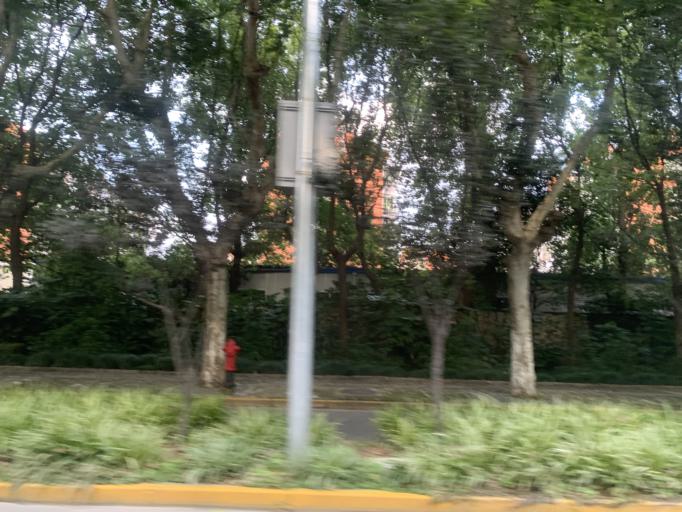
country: CN
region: Shanghai Shi
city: Huamu
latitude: 31.2129
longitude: 121.5369
